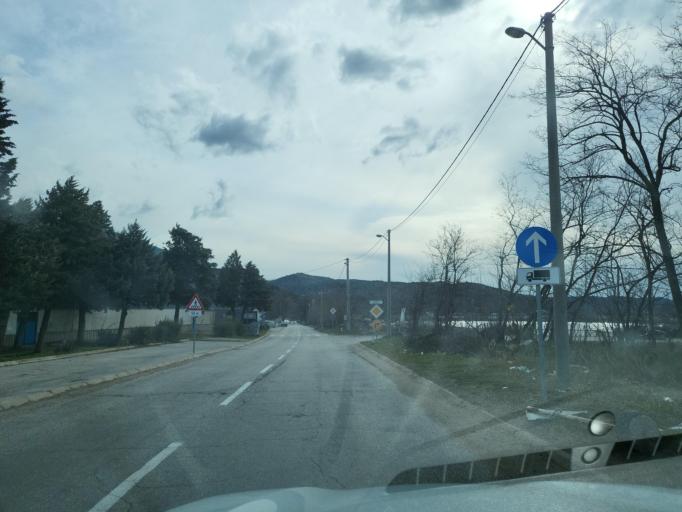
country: MK
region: Bogdanci
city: Bogdanci
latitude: 41.2026
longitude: 22.5860
